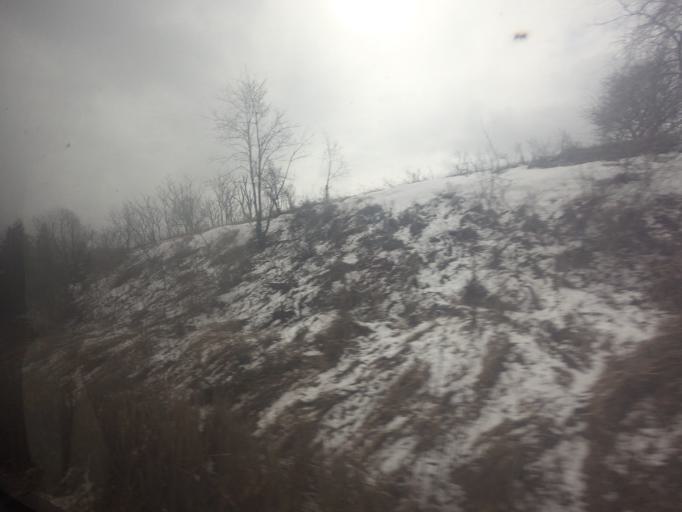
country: CA
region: Ontario
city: Cobourg
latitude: 43.9475
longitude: -78.3613
